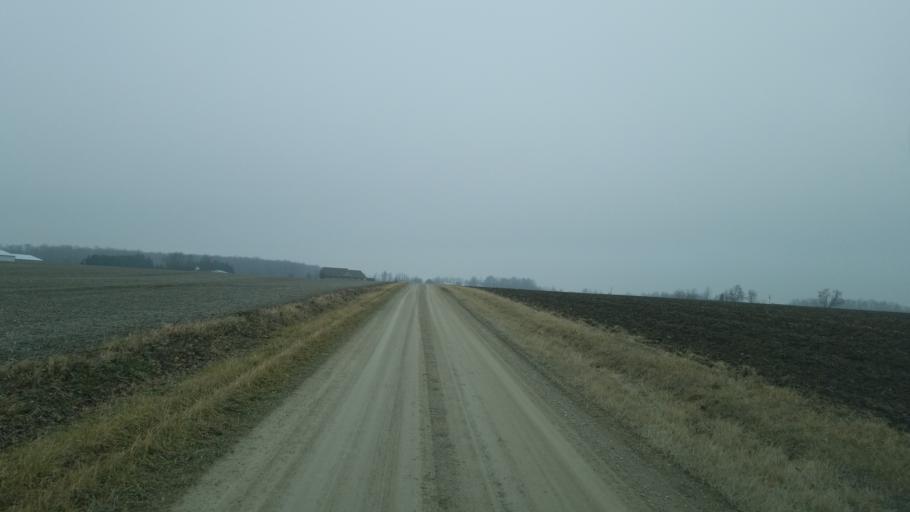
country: US
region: Indiana
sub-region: Adams County
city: Geneva
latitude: 40.5826
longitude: -84.8588
